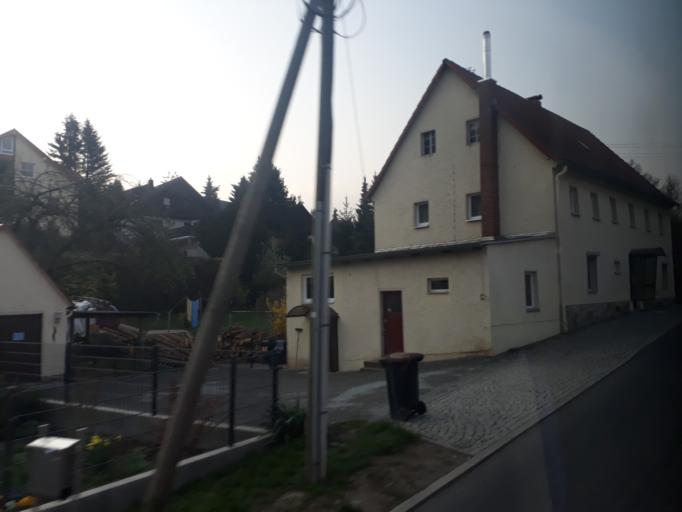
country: DE
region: Saxony
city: Reinhardtsgrimma
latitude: 50.9112
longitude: 13.7883
